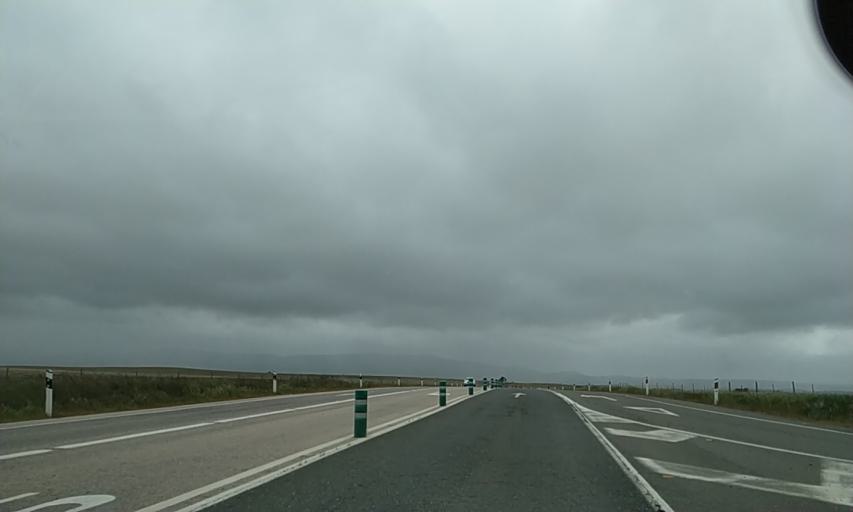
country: ES
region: Extremadura
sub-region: Provincia de Caceres
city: Malpartida de Caceres
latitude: 39.3626
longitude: -6.4623
